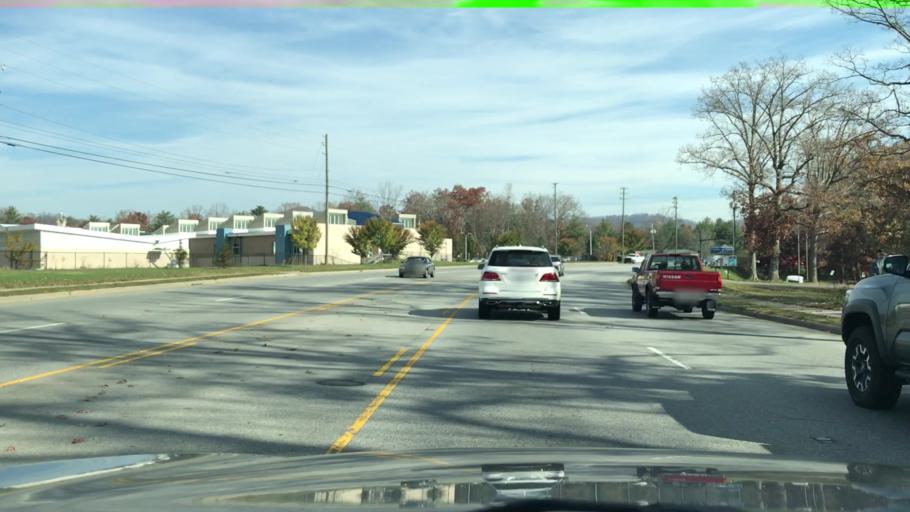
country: US
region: North Carolina
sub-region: Buncombe County
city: Royal Pines
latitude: 35.4824
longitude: -82.5408
